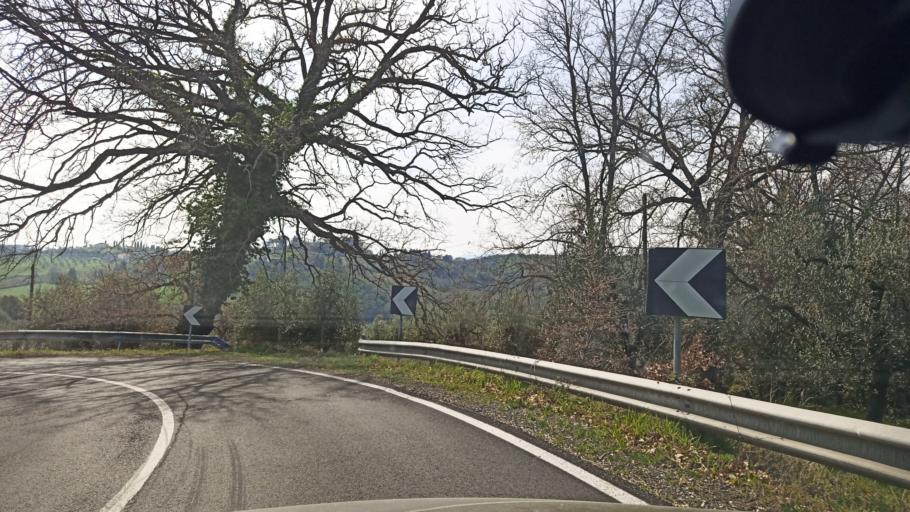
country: IT
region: Latium
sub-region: Provincia di Rieti
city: Torri in Sabina
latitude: 42.3300
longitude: 12.6442
